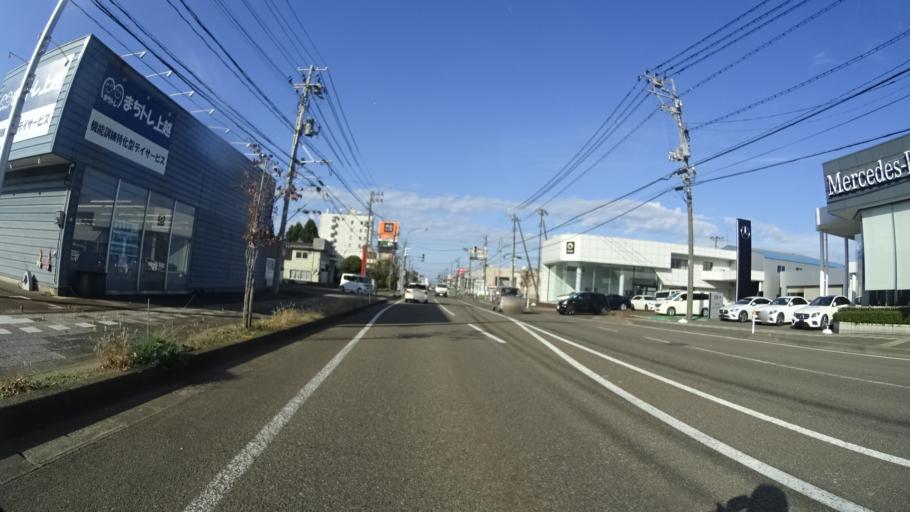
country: JP
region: Niigata
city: Joetsu
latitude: 37.1501
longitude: 138.2390
